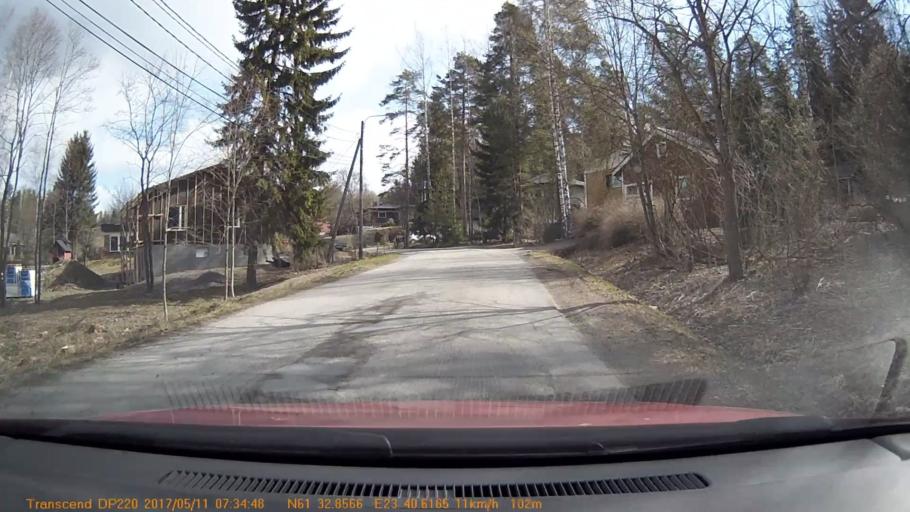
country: FI
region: Pirkanmaa
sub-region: Tampere
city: Yloejaervi
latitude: 61.5476
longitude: 23.6769
